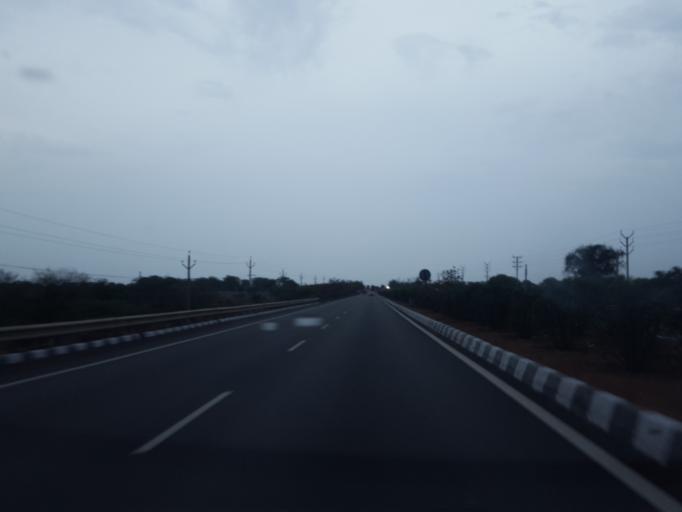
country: IN
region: Telangana
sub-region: Mahbubnagar
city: Farrukhnagar
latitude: 17.1240
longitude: 78.2751
